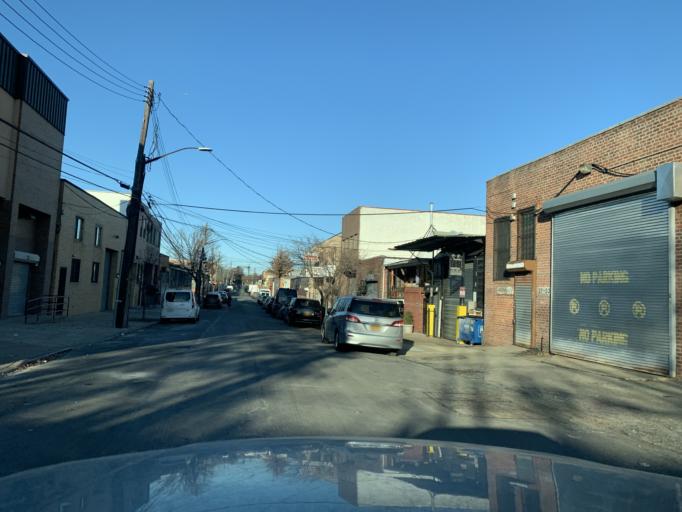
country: US
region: New York
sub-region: Queens County
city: Long Island City
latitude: 40.7498
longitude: -73.9075
